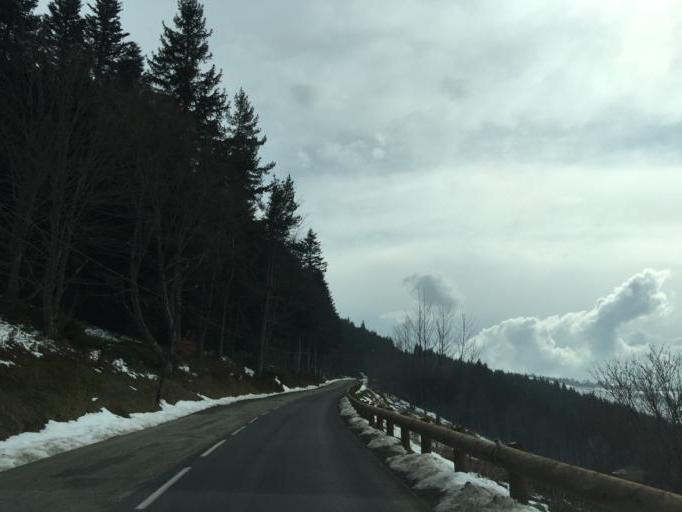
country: FR
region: Rhone-Alpes
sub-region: Departement de la Loire
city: Bourg-Argental
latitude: 45.3797
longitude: 4.5283
